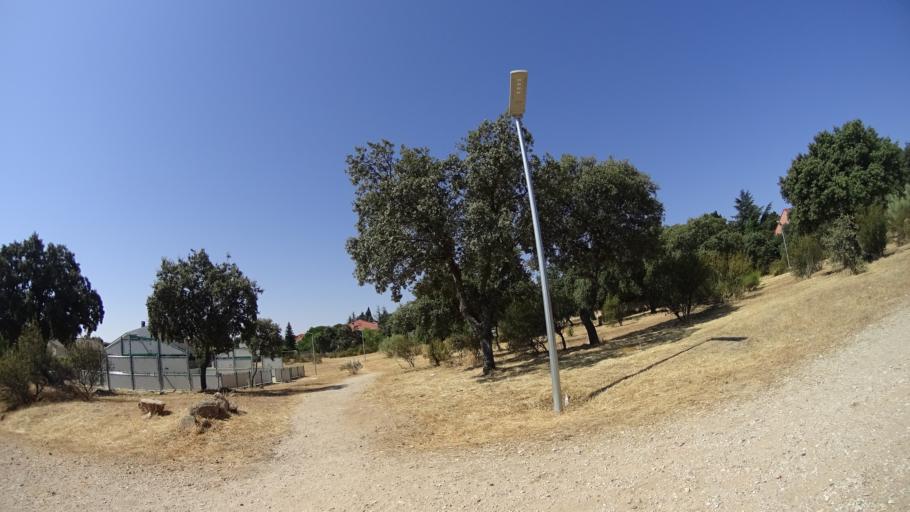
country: ES
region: Madrid
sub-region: Provincia de Madrid
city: Galapagar
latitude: 40.5935
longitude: -3.9801
